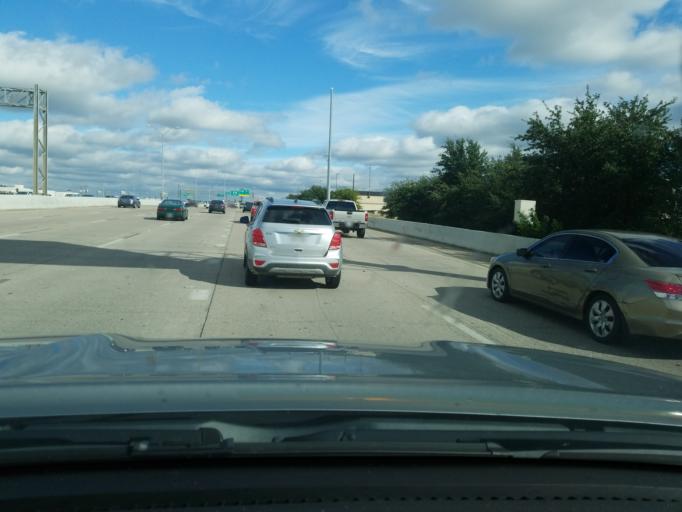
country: US
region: Texas
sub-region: Tarrant County
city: Fort Worth
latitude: 32.7447
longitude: -97.3312
